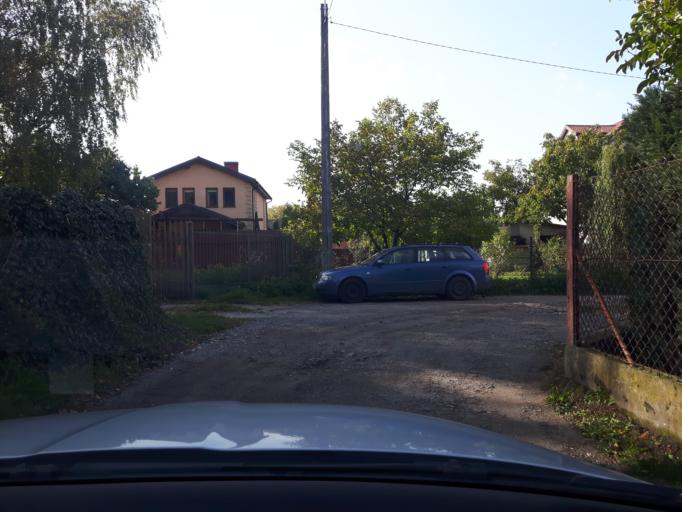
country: PL
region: Masovian Voivodeship
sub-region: Powiat wolominski
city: Zabki
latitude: 52.2899
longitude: 21.1051
